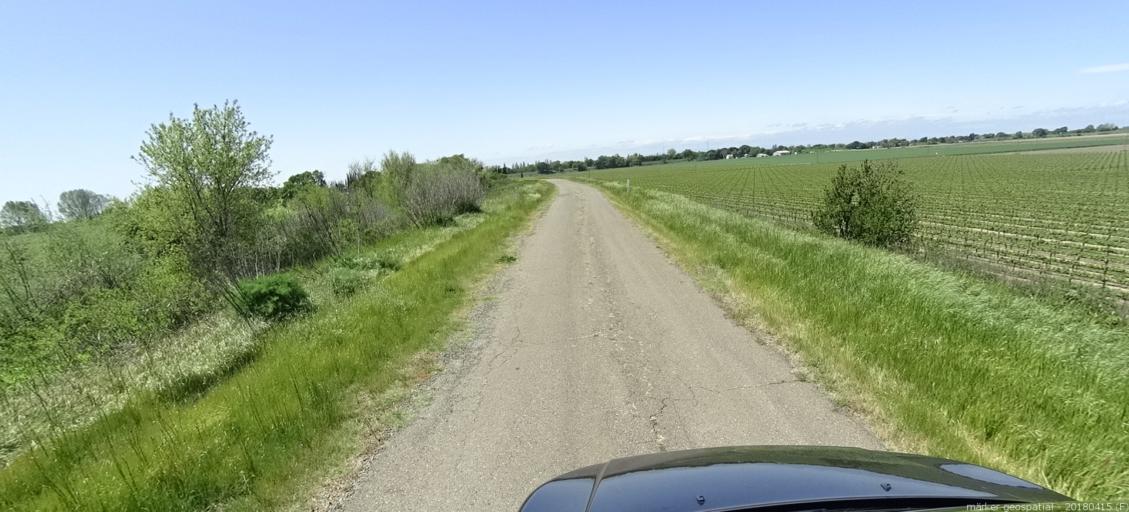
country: US
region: California
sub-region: Sacramento County
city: Walnut Grove
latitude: 38.2625
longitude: -121.5905
